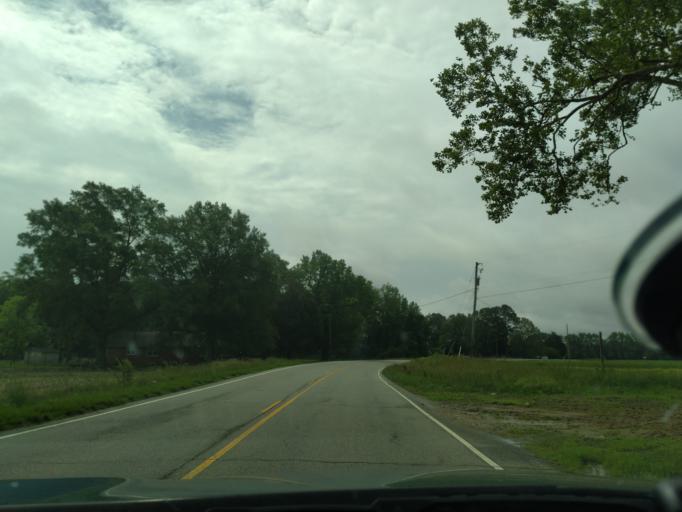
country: US
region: North Carolina
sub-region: Washington County
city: Plymouth
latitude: 35.8912
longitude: -76.6069
